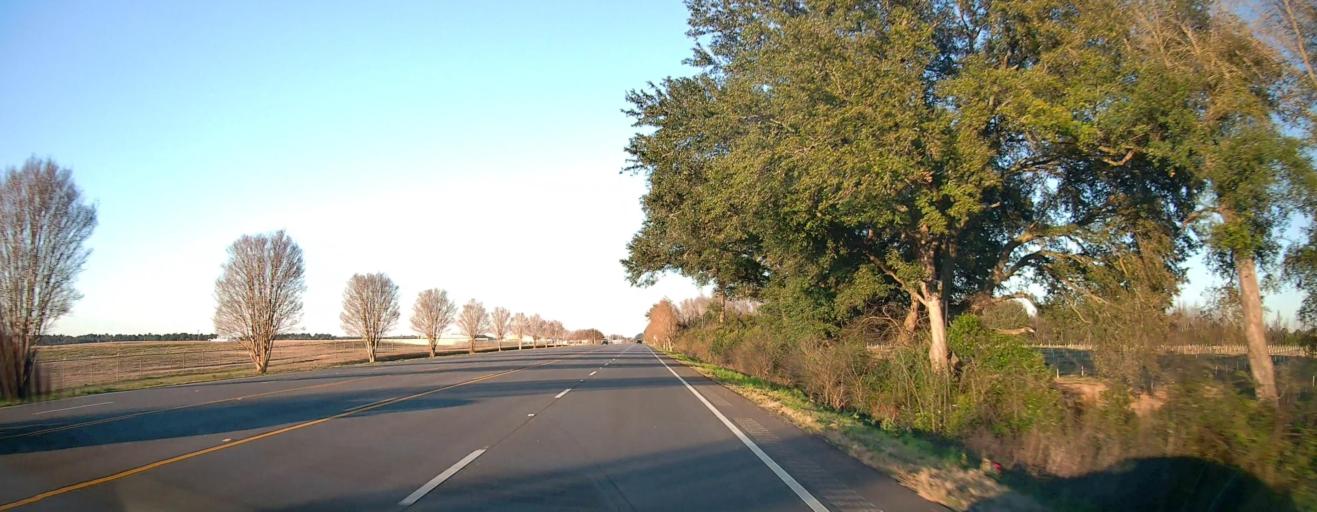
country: US
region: Georgia
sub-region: Dougherty County
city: Albany
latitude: 31.5260
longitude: -84.1918
